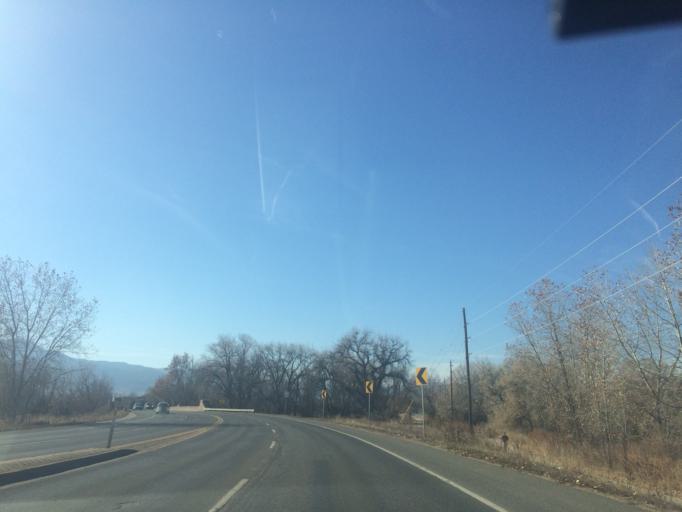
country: US
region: Colorado
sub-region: Boulder County
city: Boulder
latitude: 40.0293
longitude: -105.2216
